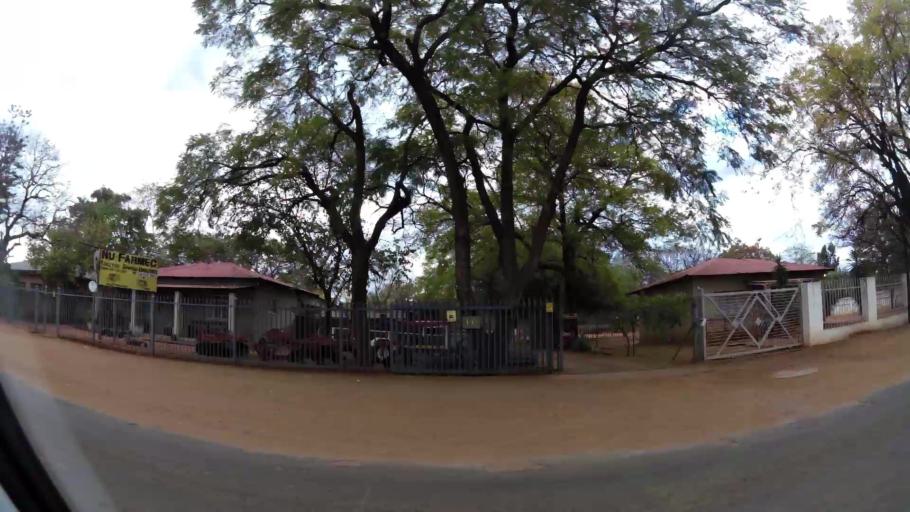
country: ZA
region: Limpopo
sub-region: Waterberg District Municipality
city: Modimolle
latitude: -24.5225
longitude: 28.7091
